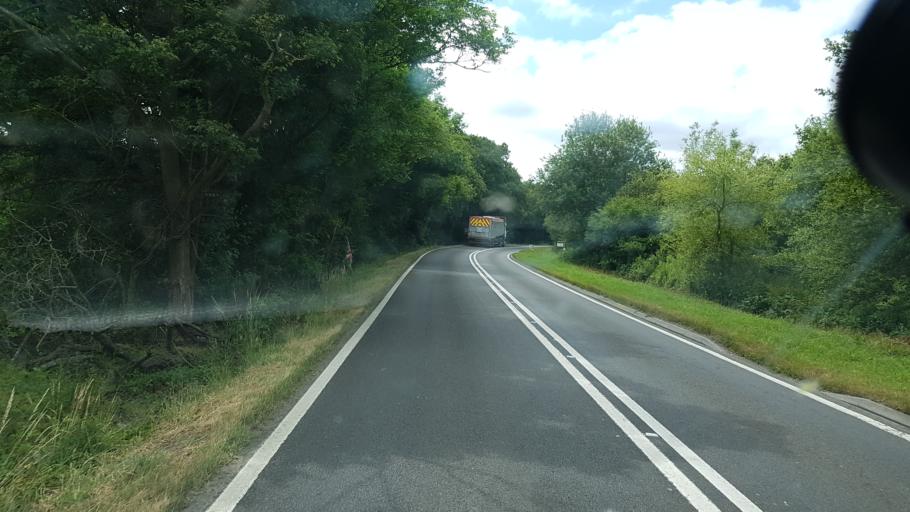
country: GB
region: England
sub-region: Surrey
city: Lingfield
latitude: 51.1789
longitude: -0.0468
